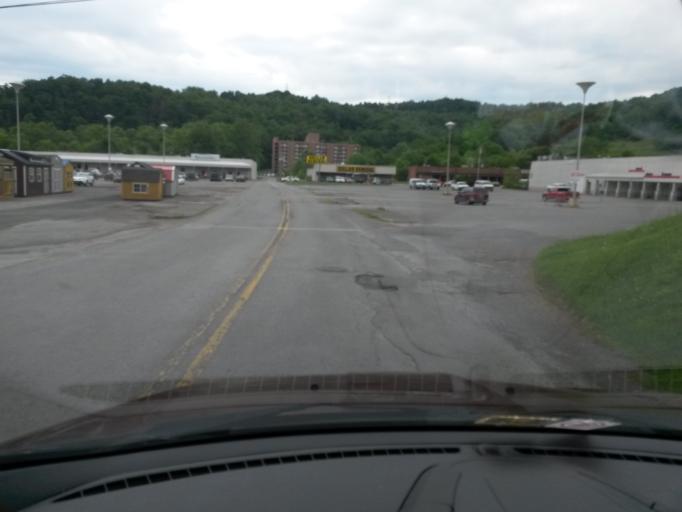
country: US
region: West Virginia
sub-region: Lewis County
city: Weston
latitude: 39.0368
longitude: -80.4474
